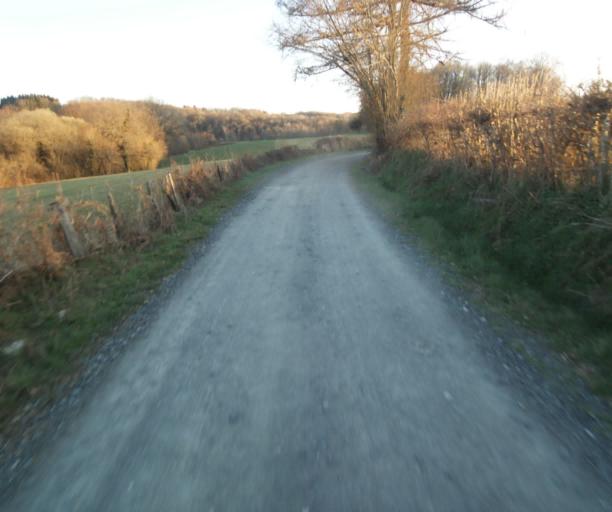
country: FR
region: Limousin
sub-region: Departement de la Correze
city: Uzerche
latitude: 45.3600
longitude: 1.6106
